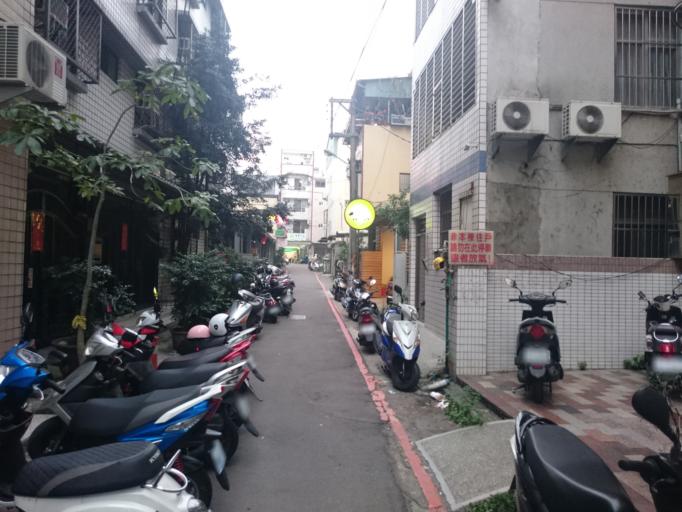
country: TW
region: Taiwan
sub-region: Taichung City
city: Taichung
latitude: 24.1813
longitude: 120.6455
